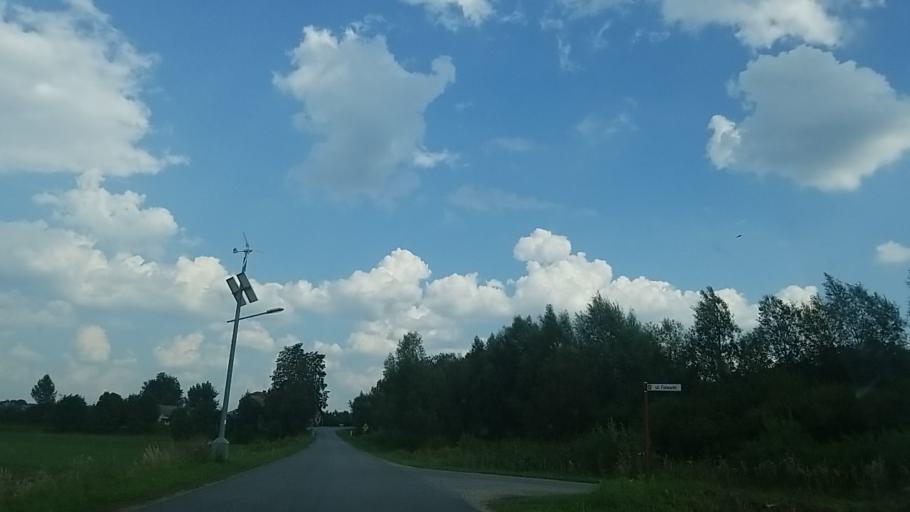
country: PL
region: Lublin Voivodeship
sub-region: Powiat bilgorajski
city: Goraj
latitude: 50.7242
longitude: 22.6555
